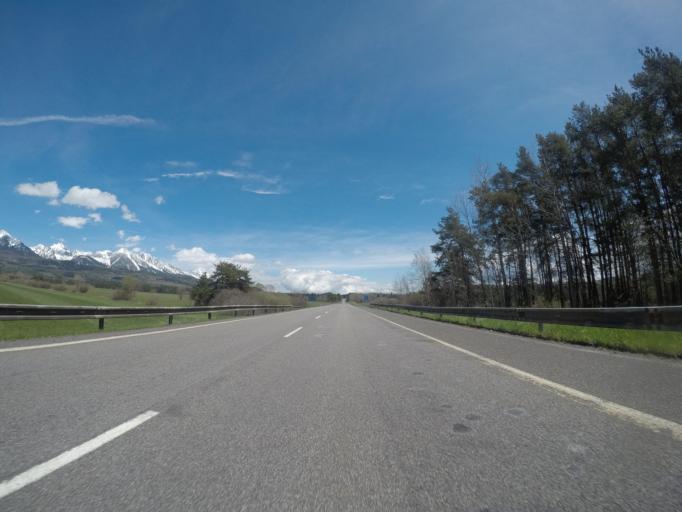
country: SK
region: Presovsky
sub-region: Okres Poprad
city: Strba
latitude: 49.0780
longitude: 20.0294
